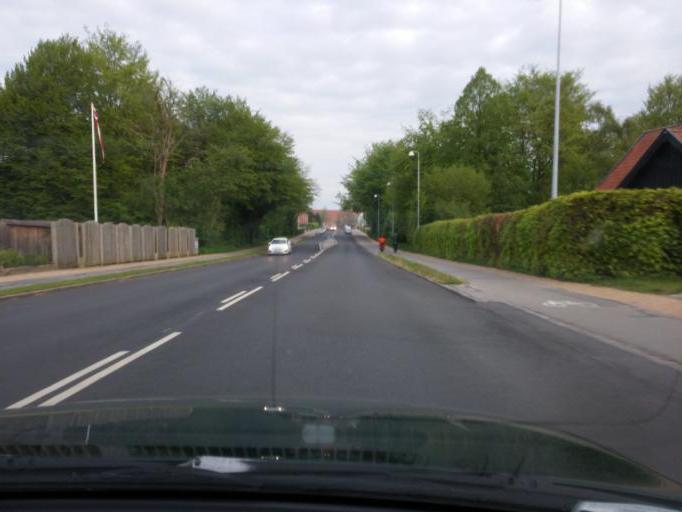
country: DK
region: South Denmark
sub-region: Odense Kommune
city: Odense
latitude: 55.3887
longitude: 10.4137
